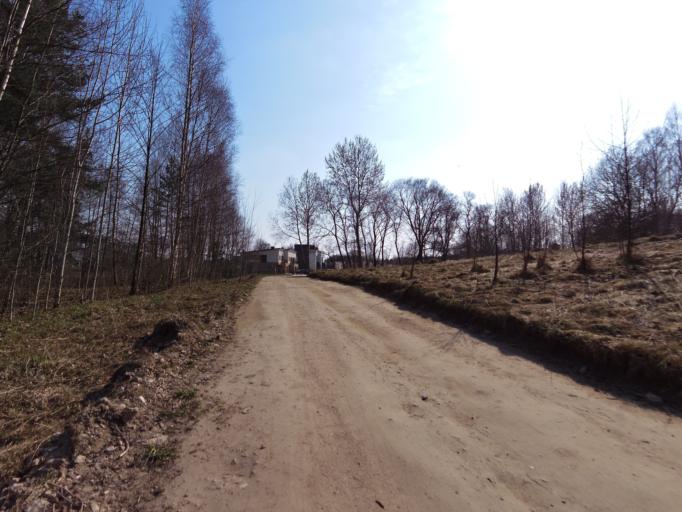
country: LT
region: Vilnius County
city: Pilaite
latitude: 54.6955
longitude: 25.1731
